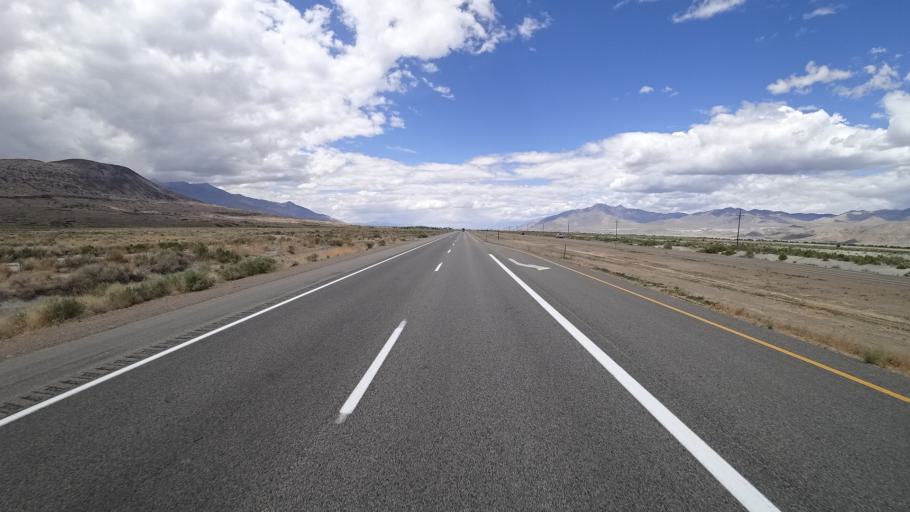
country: US
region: California
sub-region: Inyo County
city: Big Pine
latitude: 37.0962
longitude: -118.2502
